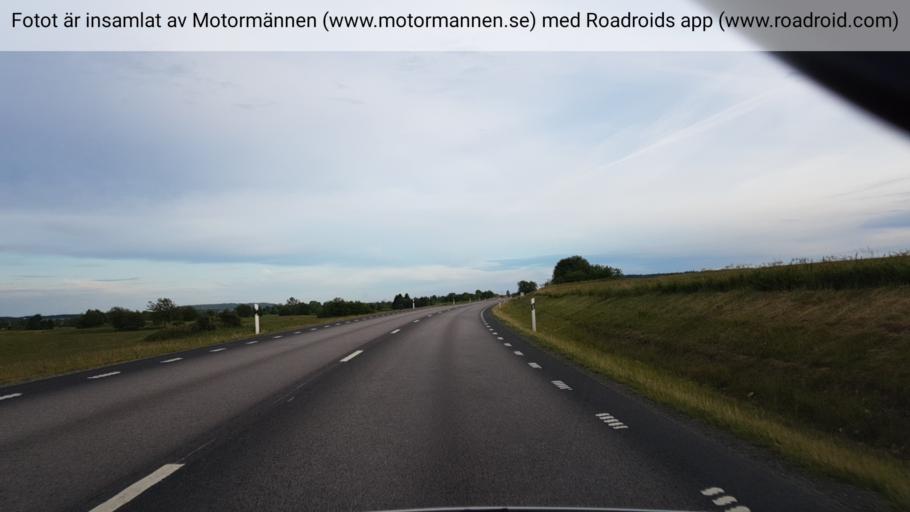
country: SE
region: Vaestra Goetaland
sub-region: Falkopings Kommun
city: Falkoeping
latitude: 58.2223
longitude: 13.5651
